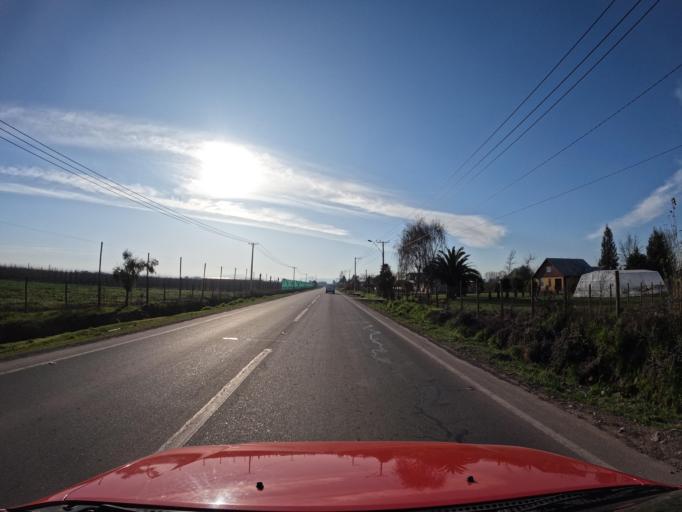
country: CL
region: Maule
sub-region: Provincia de Curico
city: Teno
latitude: -34.8976
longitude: -71.0598
